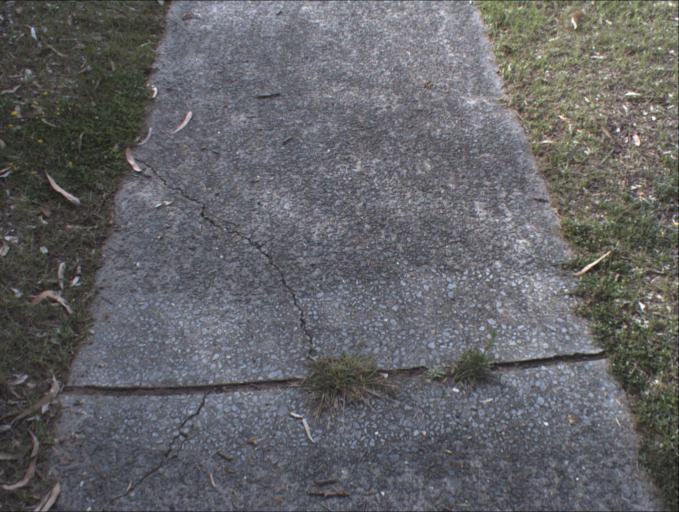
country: AU
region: Queensland
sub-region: Logan
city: Park Ridge South
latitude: -27.6862
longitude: 153.0361
